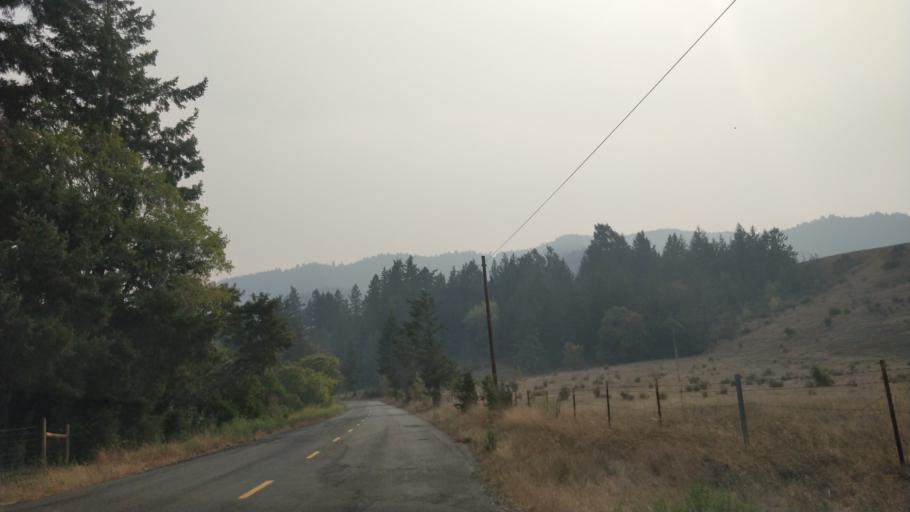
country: US
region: California
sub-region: Humboldt County
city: Rio Dell
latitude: 40.2442
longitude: -124.1639
